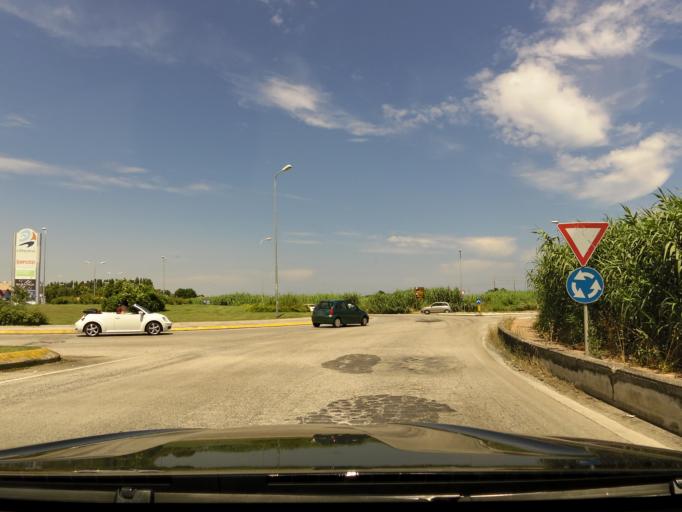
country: IT
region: The Marches
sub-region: Provincia di Pesaro e Urbino
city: Marotta
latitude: 43.7457
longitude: 13.1746
